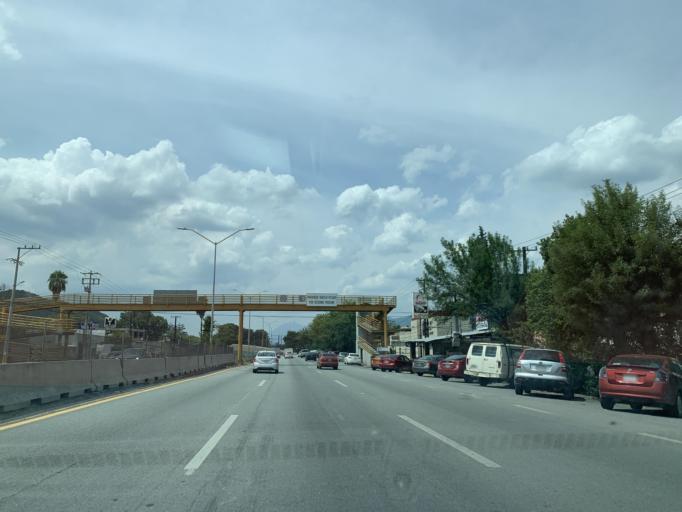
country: MX
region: Nuevo Leon
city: Santiago
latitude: 25.4067
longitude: -100.1346
